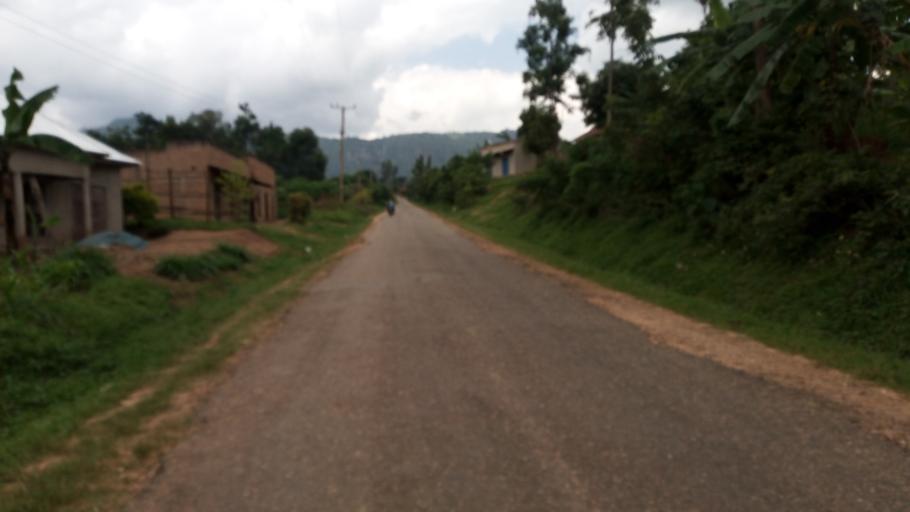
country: UG
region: Eastern Region
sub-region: Mbale District
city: Mbale
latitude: 1.0718
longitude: 34.2057
